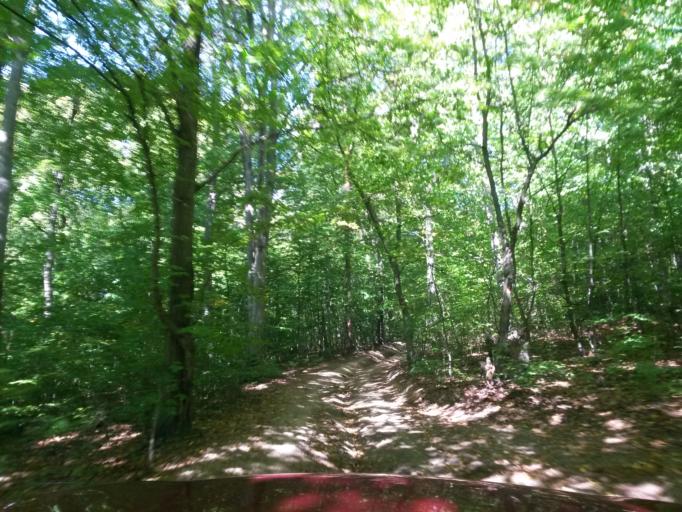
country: SK
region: Presovsky
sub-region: Okres Presov
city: Presov
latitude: 48.9740
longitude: 21.1489
